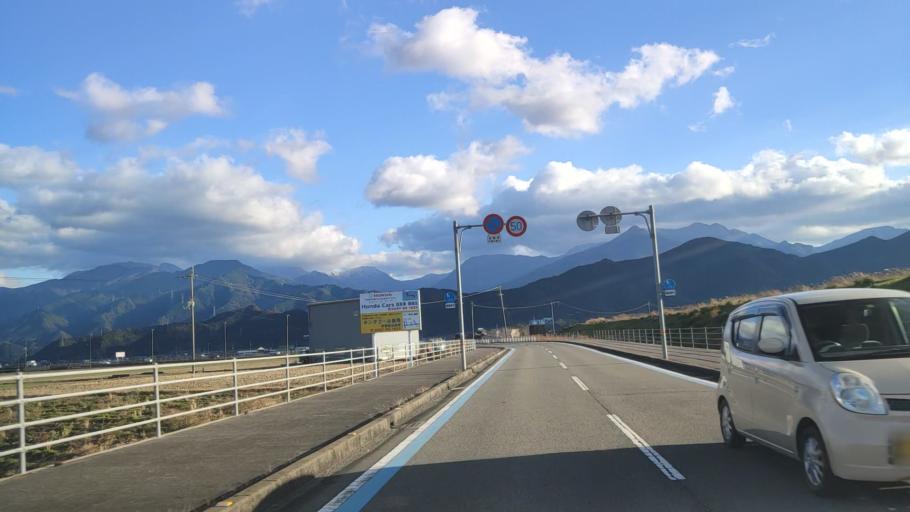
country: JP
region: Ehime
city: Saijo
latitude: 33.9084
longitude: 133.1423
